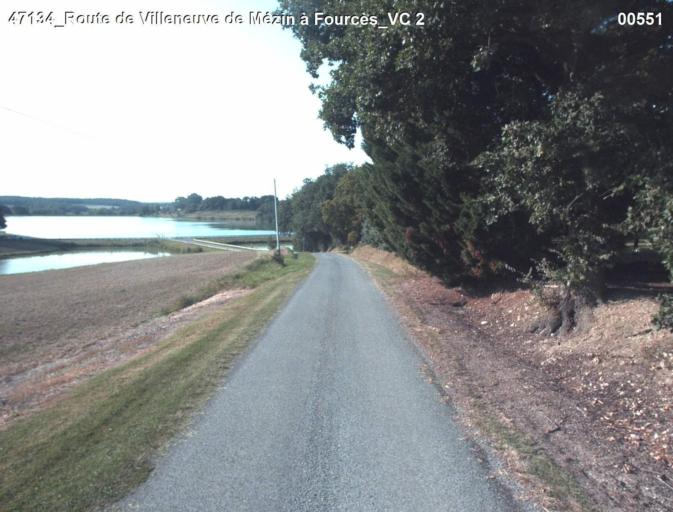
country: FR
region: Aquitaine
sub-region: Departement du Lot-et-Garonne
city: Mezin
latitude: 44.0128
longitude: 0.2473
